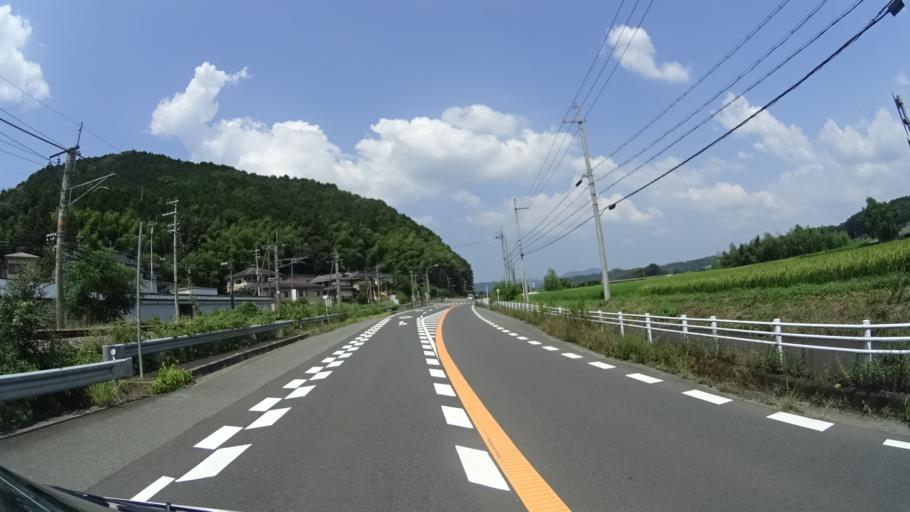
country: JP
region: Kyoto
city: Fukuchiyama
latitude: 35.2785
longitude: 135.1368
